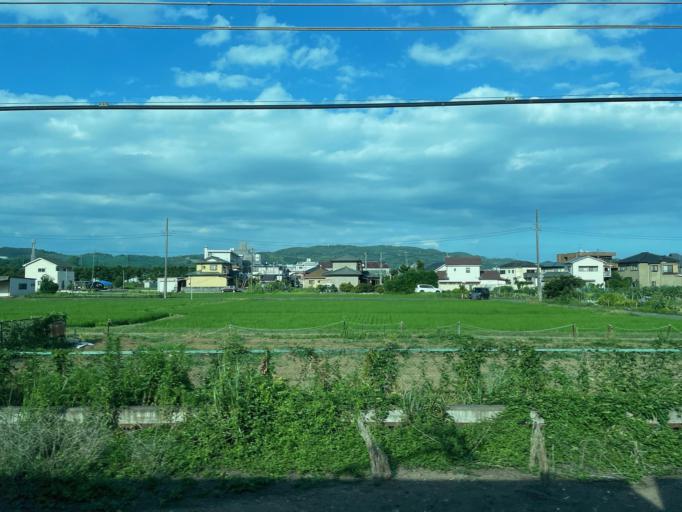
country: JP
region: Kanagawa
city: Odawara
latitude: 35.3129
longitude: 139.1422
